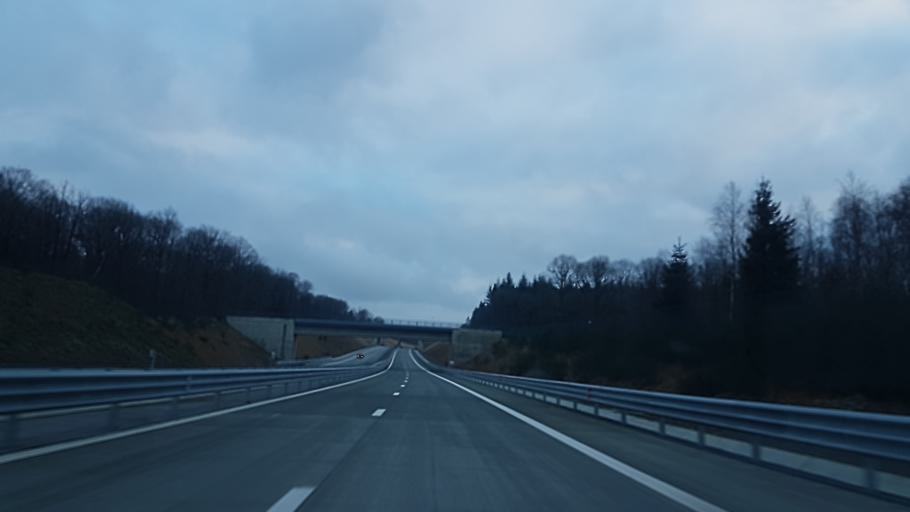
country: BE
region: Wallonia
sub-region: Province de Namur
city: Couvin
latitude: 50.0059
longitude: 4.5384
